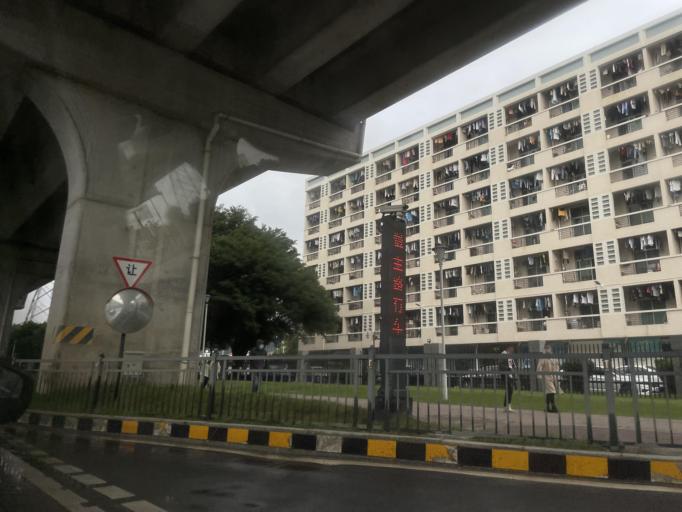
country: CN
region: Guangdong
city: Wanzai
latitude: 22.1766
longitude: 113.4916
